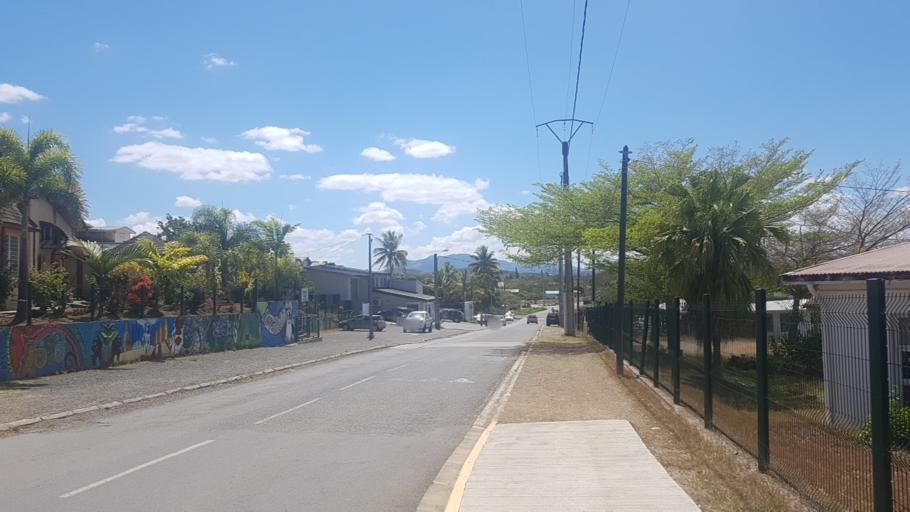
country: NC
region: North Province
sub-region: Kone
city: Kone
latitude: -21.0603
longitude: 164.8630
